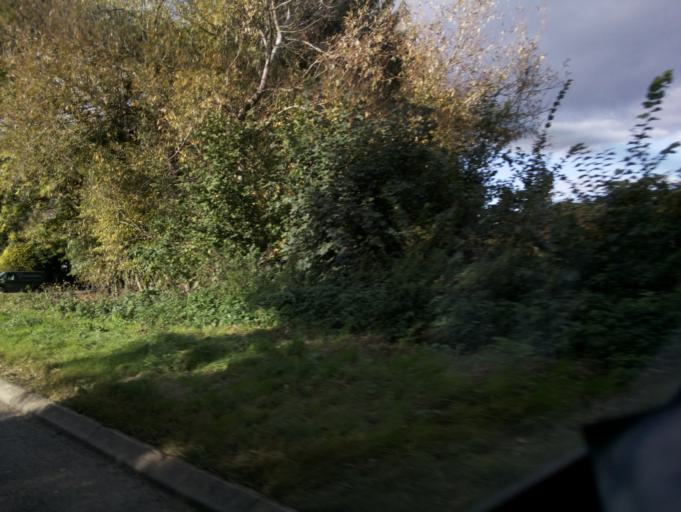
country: GB
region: England
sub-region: Herefordshire
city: Kinnersley
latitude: 52.1180
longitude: -2.9827
